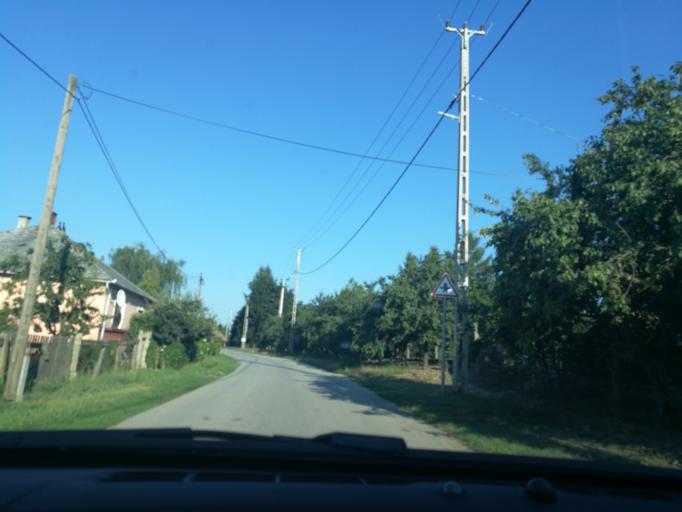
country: HU
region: Szabolcs-Szatmar-Bereg
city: Tiszabercel
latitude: 48.1682
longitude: 21.5820
